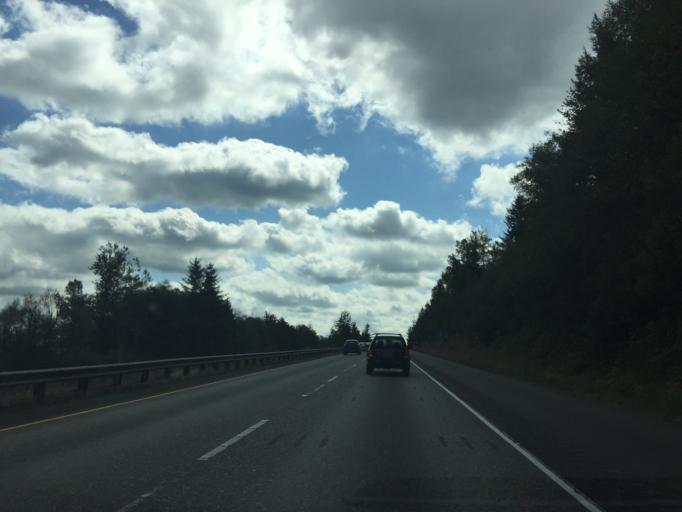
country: US
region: Washington
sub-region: Whatcom County
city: Sudden Valley
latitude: 48.6320
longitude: -122.3593
